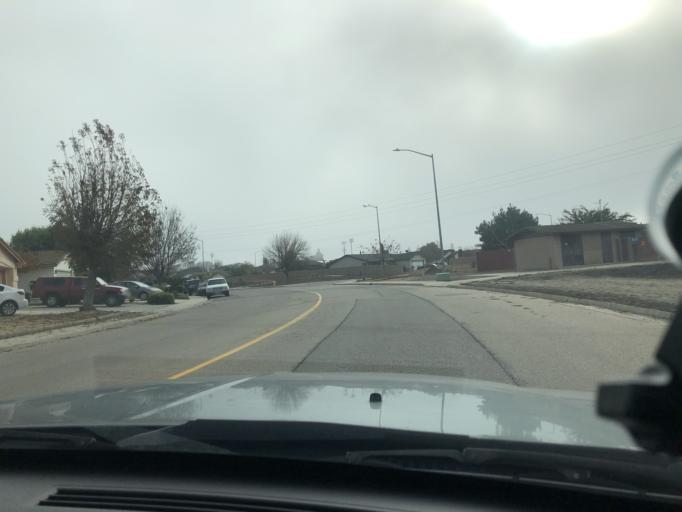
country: US
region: California
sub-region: Monterey County
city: King City
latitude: 36.2120
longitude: -121.1389
